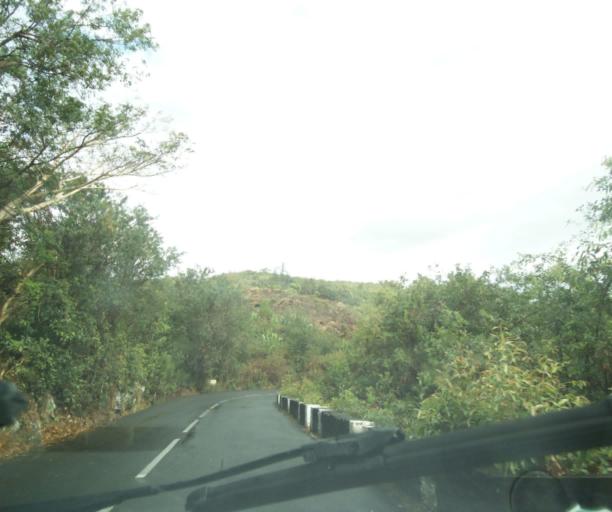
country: RE
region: Reunion
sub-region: Reunion
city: Saint-Paul
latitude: -21.0103
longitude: 55.3140
